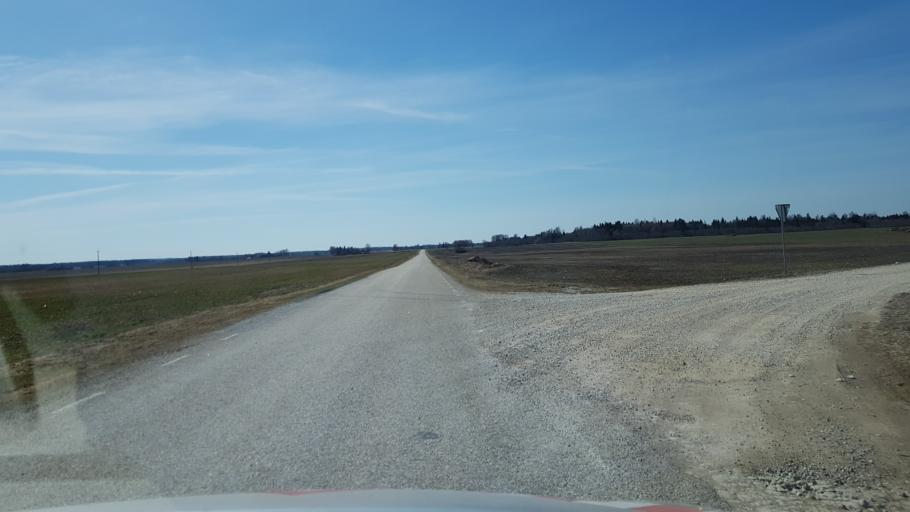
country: EE
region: Laeaene-Virumaa
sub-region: Vinni vald
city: Vinni
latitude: 59.0852
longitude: 26.4627
